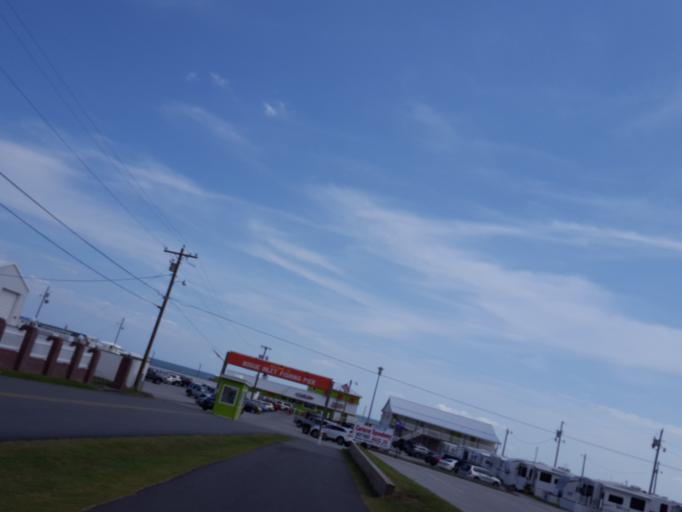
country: US
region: North Carolina
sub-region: Carteret County
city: Cape Carteret
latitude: 34.6624
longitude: -77.0344
